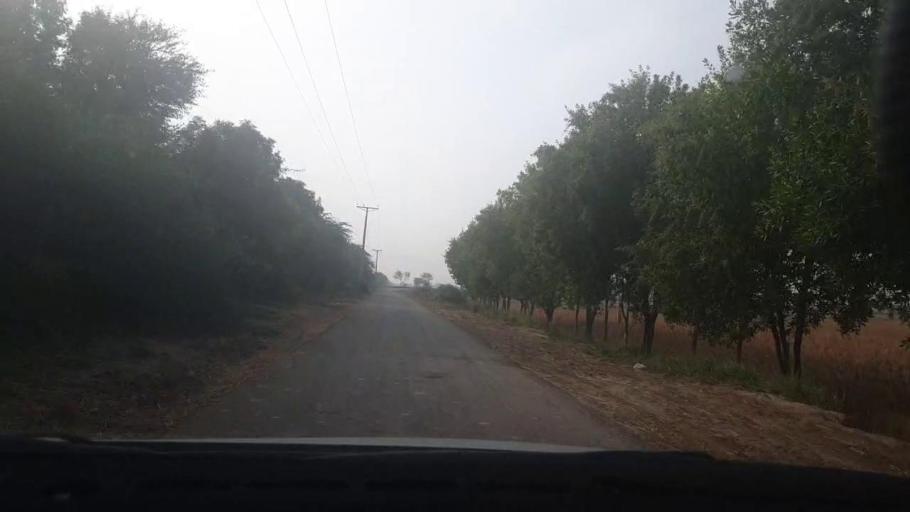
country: PK
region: Sindh
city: Tando Muhammad Khan
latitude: 25.0885
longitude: 68.5163
